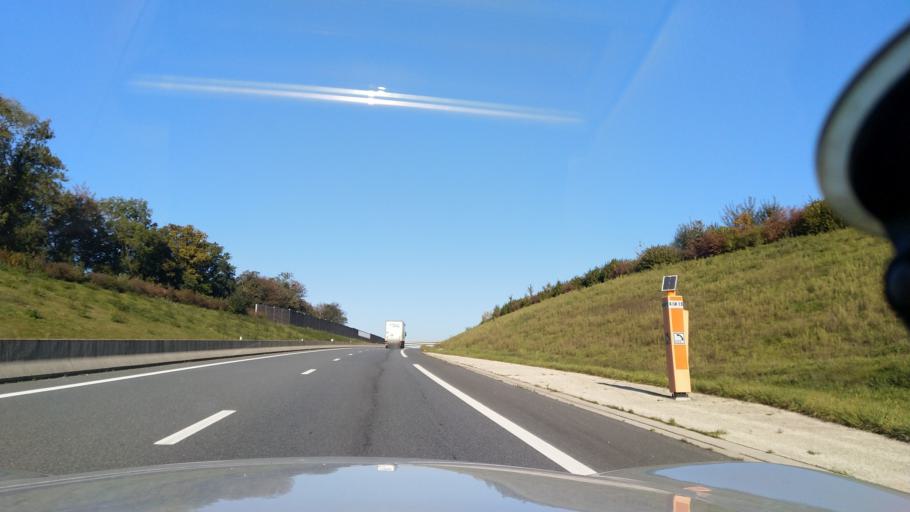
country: FR
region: Haute-Normandie
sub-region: Departement de la Seine-Maritime
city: Villers-Ecalles
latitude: 49.5376
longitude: 0.9346
